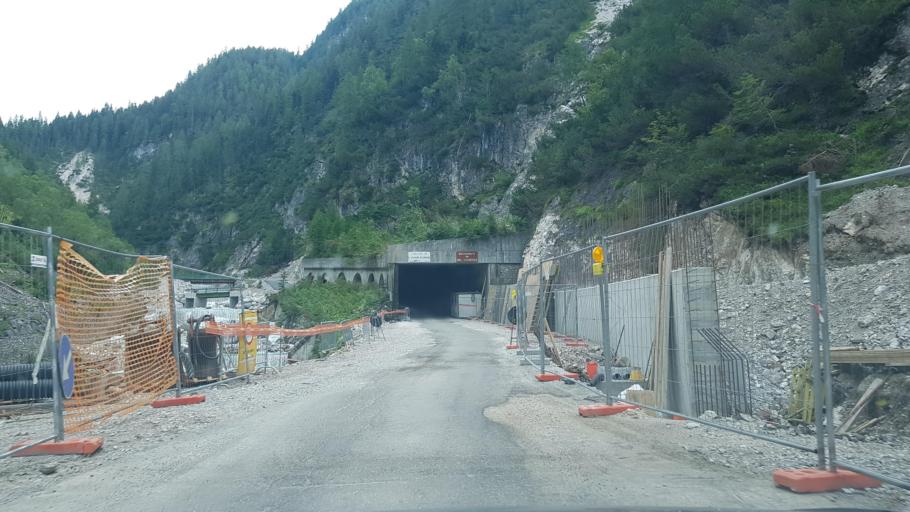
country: IT
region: Veneto
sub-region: Provincia di Belluno
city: San Pietro di Cadore
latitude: 46.5914
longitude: 12.6299
